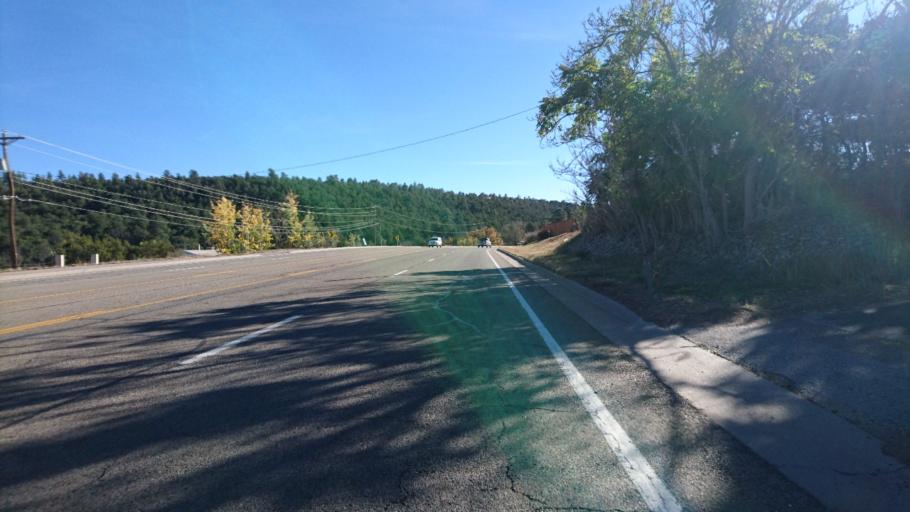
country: US
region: New Mexico
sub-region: Bernalillo County
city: Sandia Knolls
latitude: 35.1591
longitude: -106.3517
